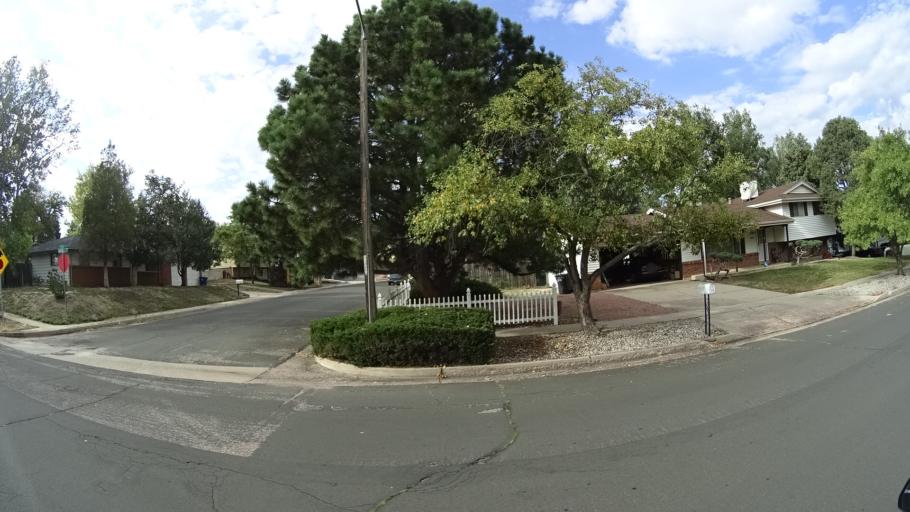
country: US
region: Colorado
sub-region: El Paso County
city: Cimarron Hills
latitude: 38.8438
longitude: -104.7509
